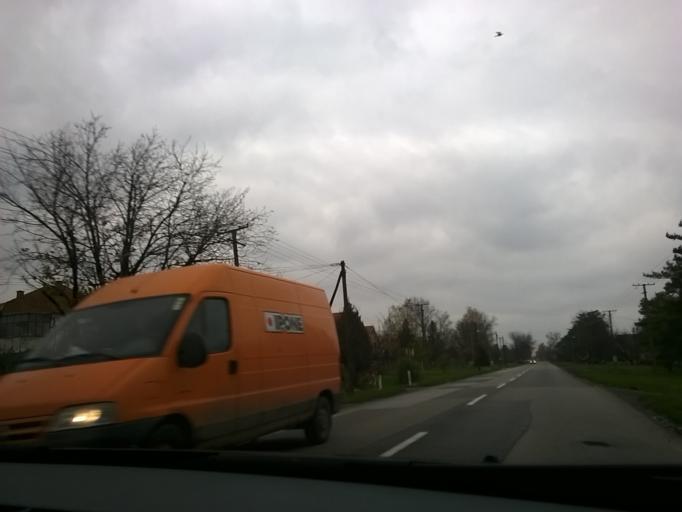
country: RS
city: Centa
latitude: 45.1149
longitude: 20.3856
